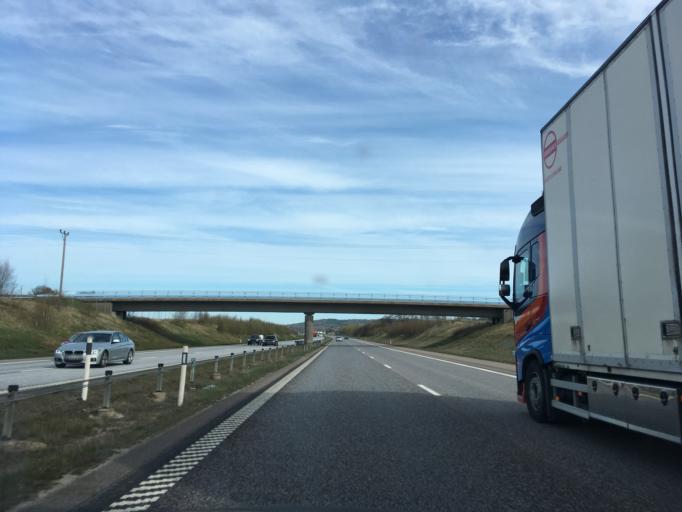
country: SE
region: Halland
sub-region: Halmstads Kommun
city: Getinge
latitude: 56.7729
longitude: 12.8097
